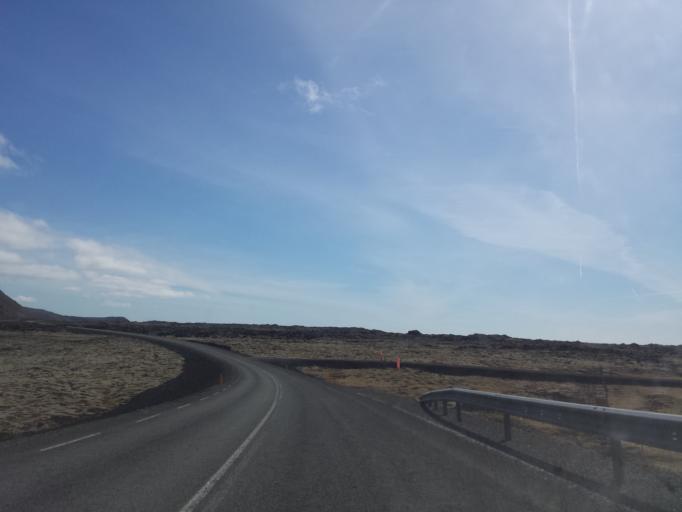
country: IS
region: Southern Peninsula
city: Grindavik
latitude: 63.8519
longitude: -22.3025
